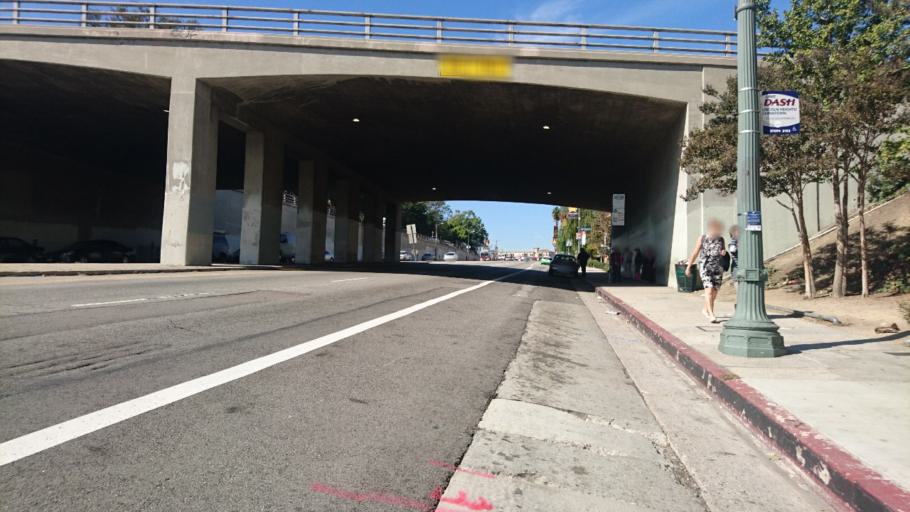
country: US
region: California
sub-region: Los Angeles County
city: Los Angeles
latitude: 34.0590
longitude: -118.2408
